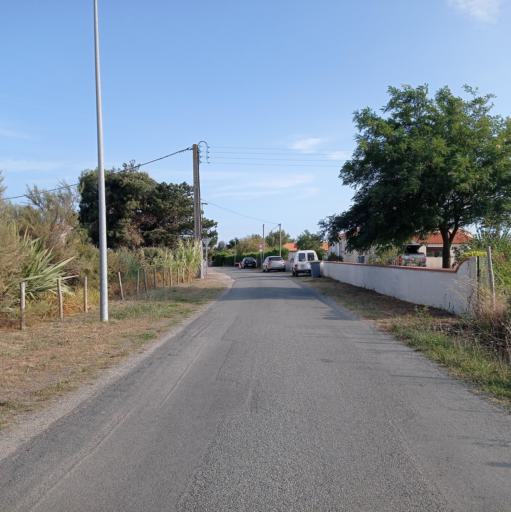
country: FR
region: Pays de la Loire
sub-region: Departement de la Vendee
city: Bretignolles-sur-Mer
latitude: 46.5953
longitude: -1.8193
